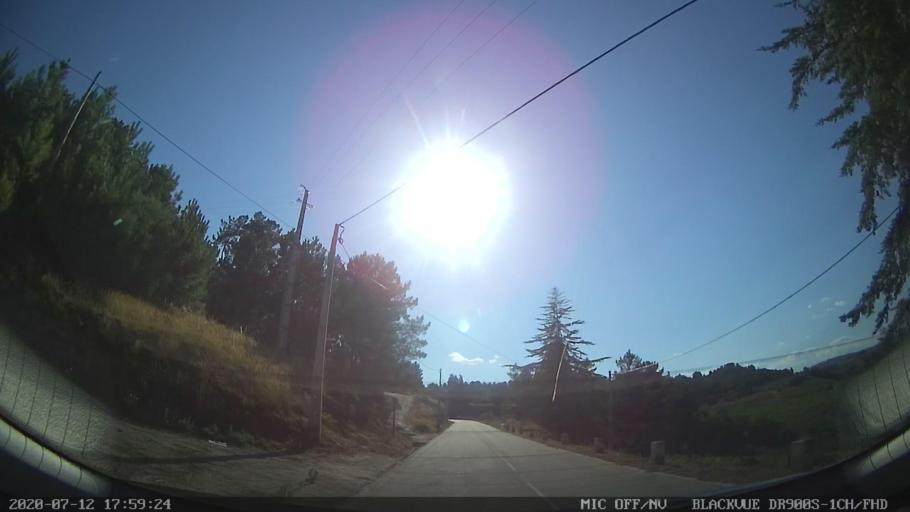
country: PT
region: Viseu
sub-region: Sao Joao da Pesqueira
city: Sao Joao da Pesqueira
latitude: 41.2623
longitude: -7.4461
